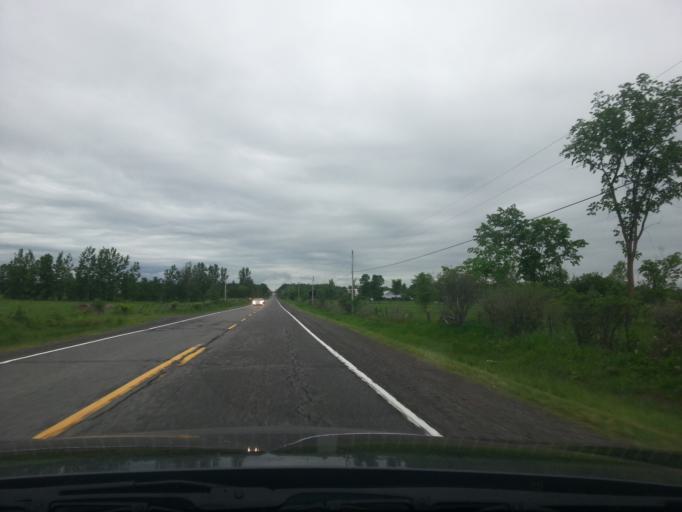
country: CA
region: Ontario
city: Bells Corners
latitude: 45.1982
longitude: -75.9377
